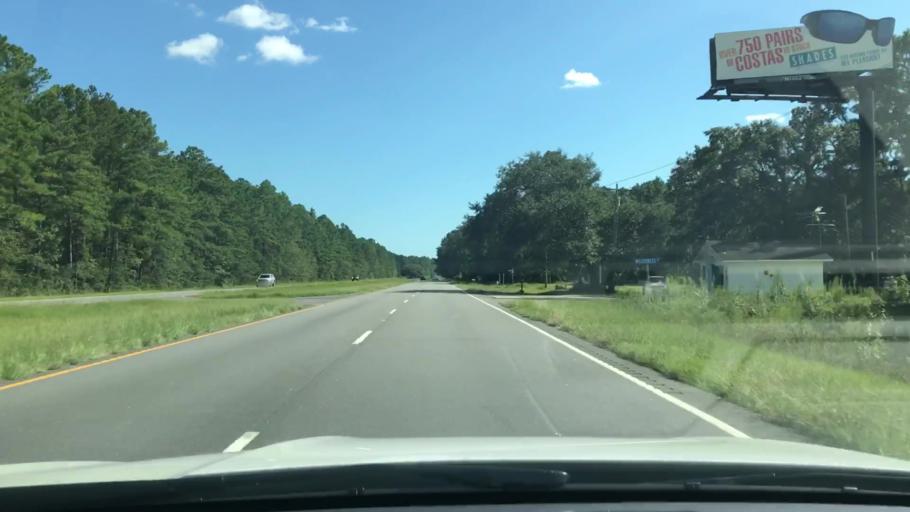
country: US
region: South Carolina
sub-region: Georgetown County
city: Georgetown
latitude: 33.2413
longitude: -79.3758
